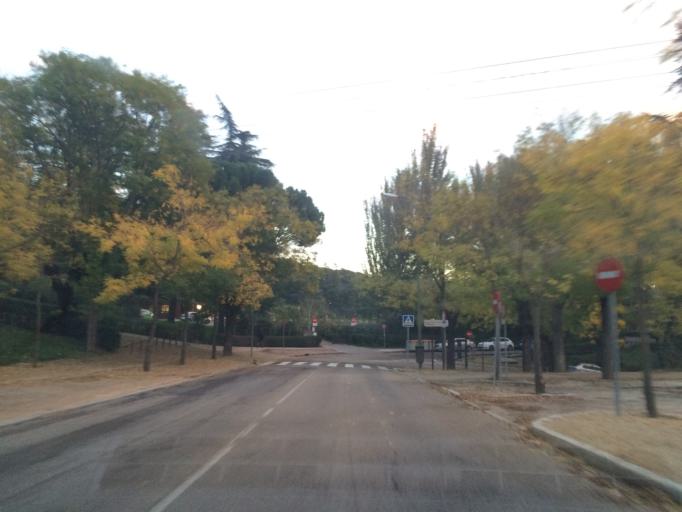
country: ES
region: Madrid
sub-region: Provincia de Madrid
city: Moncloa-Aravaca
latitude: 40.4280
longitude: -3.7232
